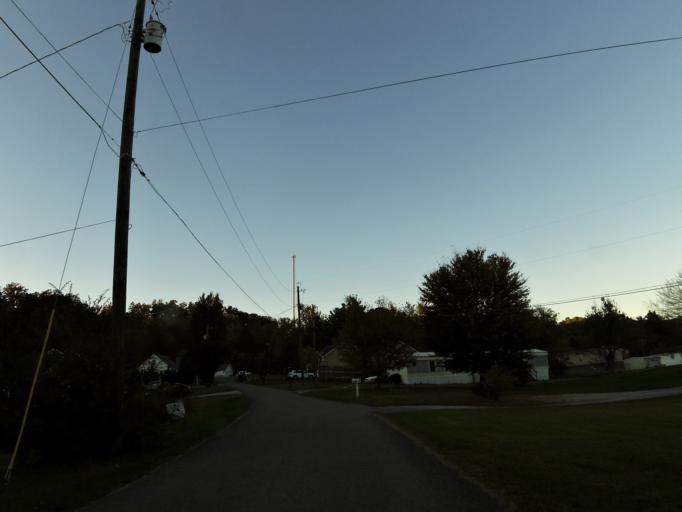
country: US
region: Tennessee
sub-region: Knox County
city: Knoxville
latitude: 36.0333
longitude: -83.9875
